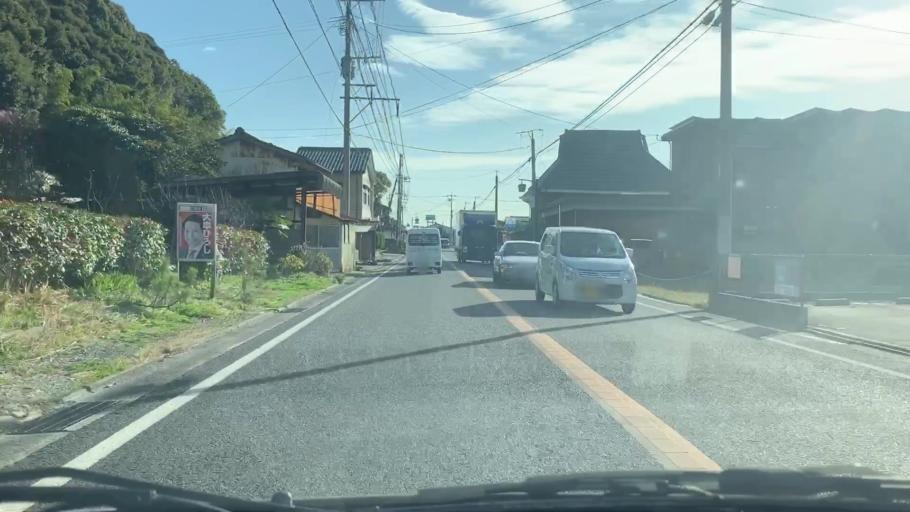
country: JP
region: Saga Prefecture
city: Takeocho-takeo
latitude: 33.2166
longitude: 130.0845
